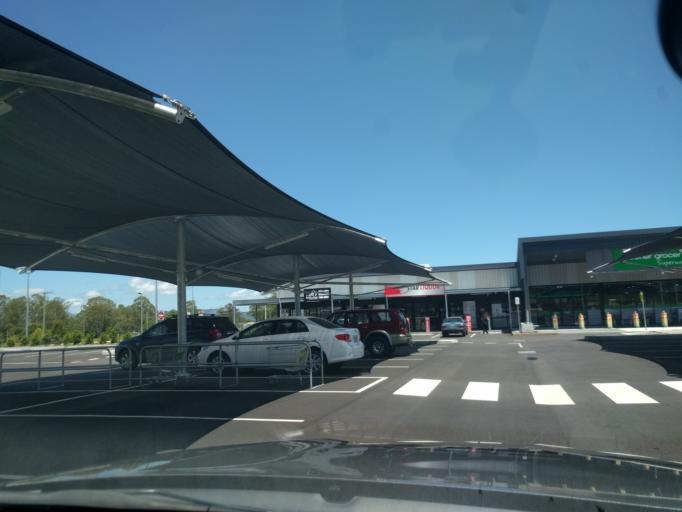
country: AU
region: Queensland
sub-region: Logan
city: Cedar Vale
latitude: -27.9930
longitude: 153.0110
